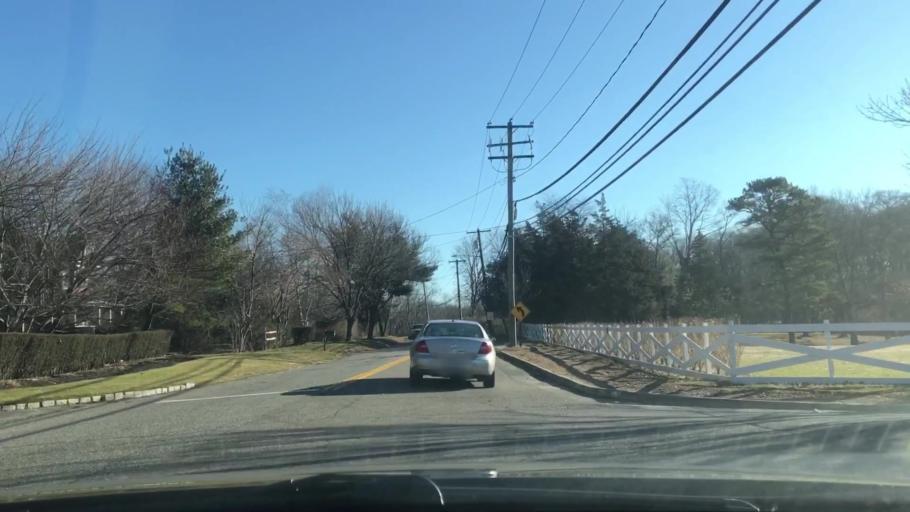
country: US
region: New York
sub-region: Suffolk County
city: Riverhead
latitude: 40.9375
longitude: -72.6718
